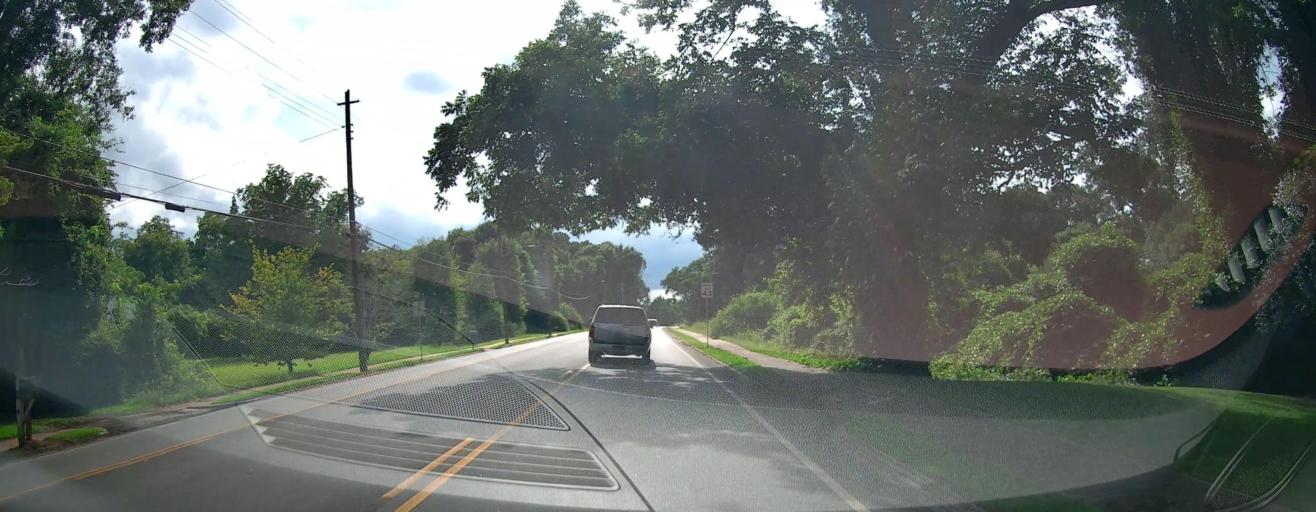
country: US
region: Georgia
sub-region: Meriwether County
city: Manchester
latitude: 32.9832
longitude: -84.5886
